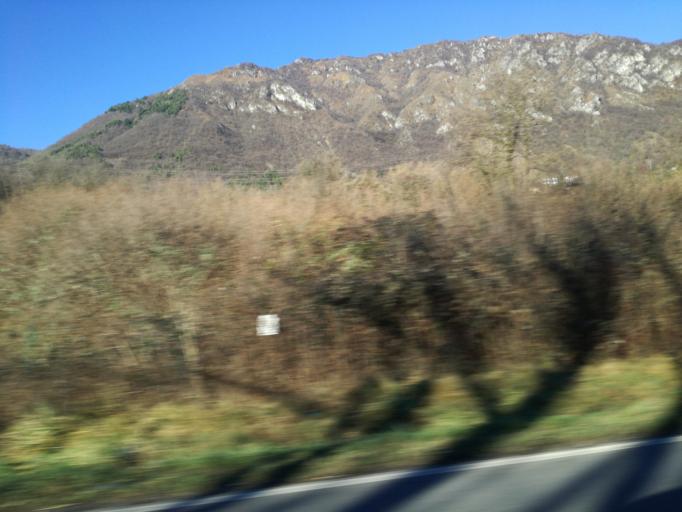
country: IT
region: Lombardy
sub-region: Provincia di Bergamo
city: Piangaiano
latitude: 45.7965
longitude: 10.0113
